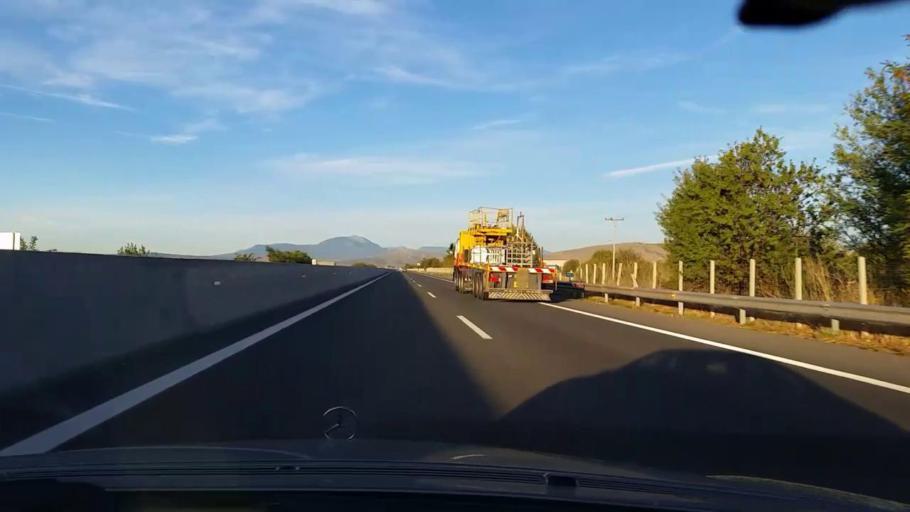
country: GR
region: Central Greece
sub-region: Nomos Voiotias
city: Thivai
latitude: 38.3701
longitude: 23.3789
